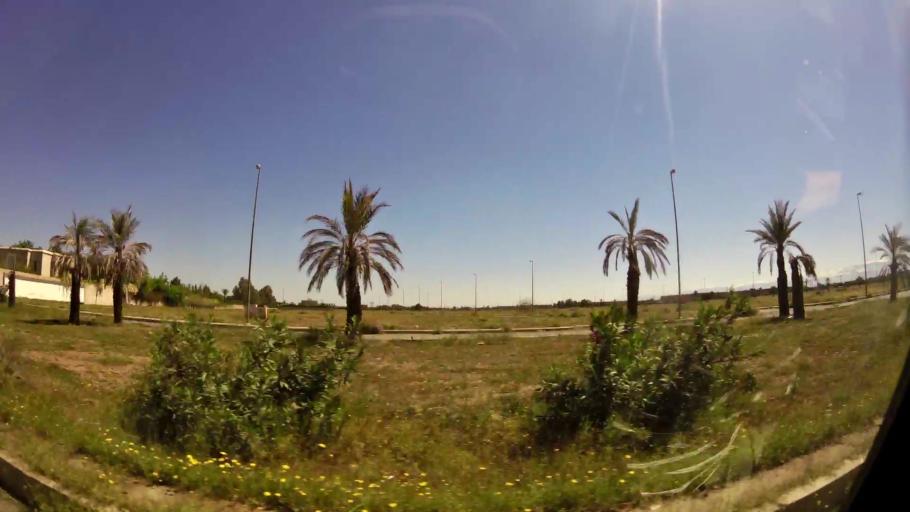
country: MA
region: Marrakech-Tensift-Al Haouz
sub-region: Marrakech
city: Marrakesh
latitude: 31.5855
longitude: -8.0055
